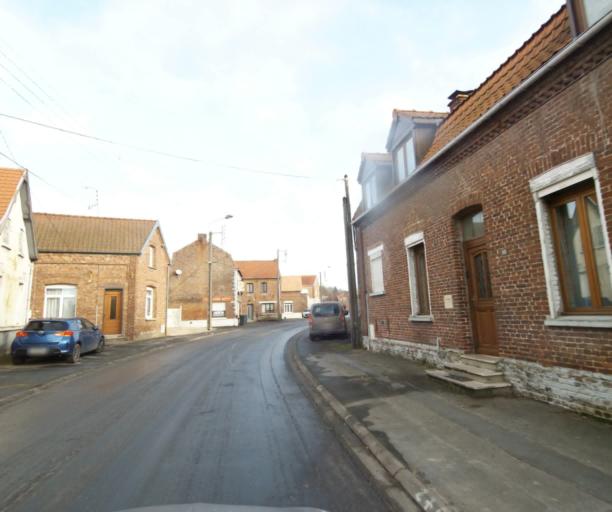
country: FR
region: Nord-Pas-de-Calais
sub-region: Departement du Nord
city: Vendegies-sur-Ecaillon
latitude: 50.2700
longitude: 3.4780
